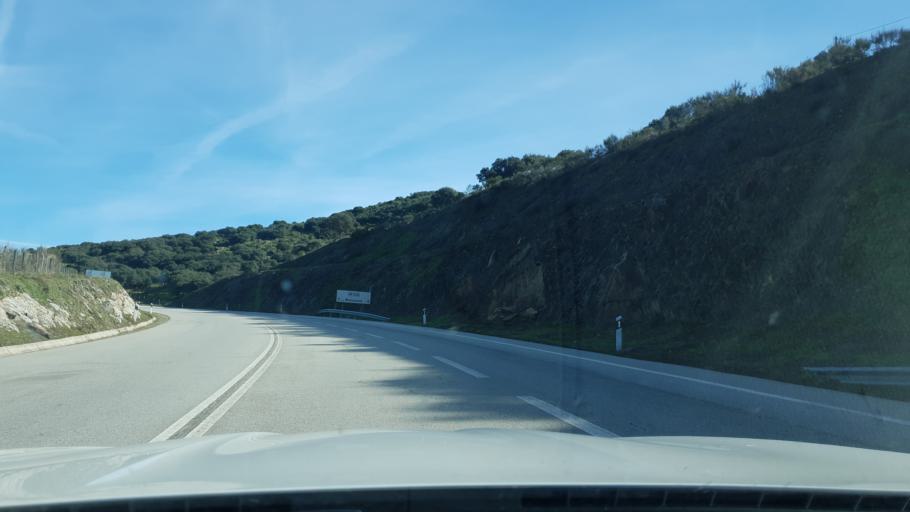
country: PT
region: Braganca
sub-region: Torre de Moncorvo
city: Torre de Moncorvo
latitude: 41.1812
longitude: -7.0988
